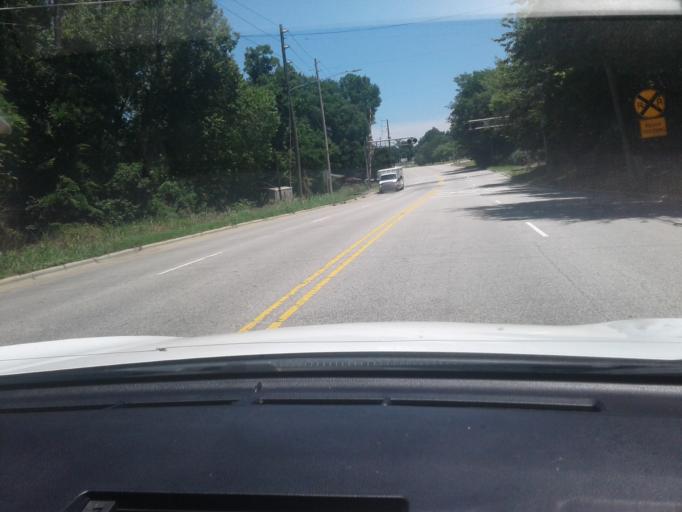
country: US
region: North Carolina
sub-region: Harnett County
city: Lillington
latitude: 35.3924
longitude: -78.8139
